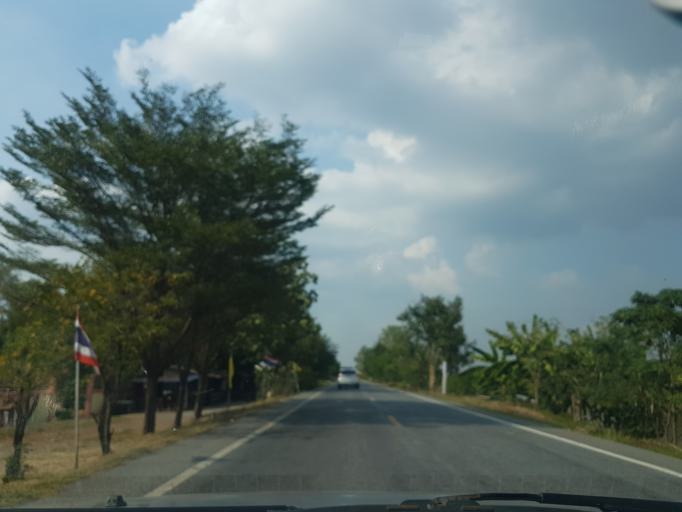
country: TH
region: Phra Nakhon Si Ayutthaya
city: Phachi
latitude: 14.4406
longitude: 100.7679
